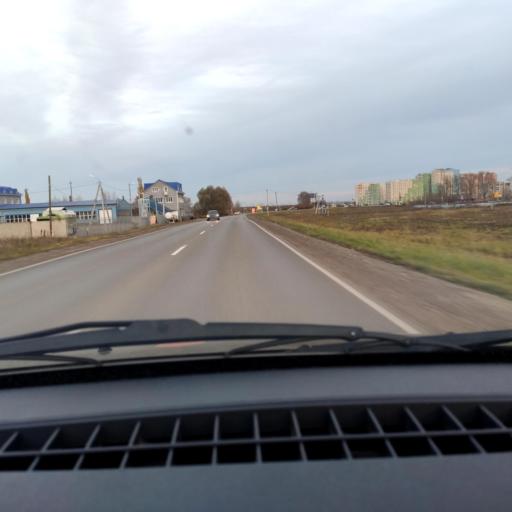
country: RU
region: Bashkortostan
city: Mikhaylovka
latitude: 54.7991
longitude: 55.8533
